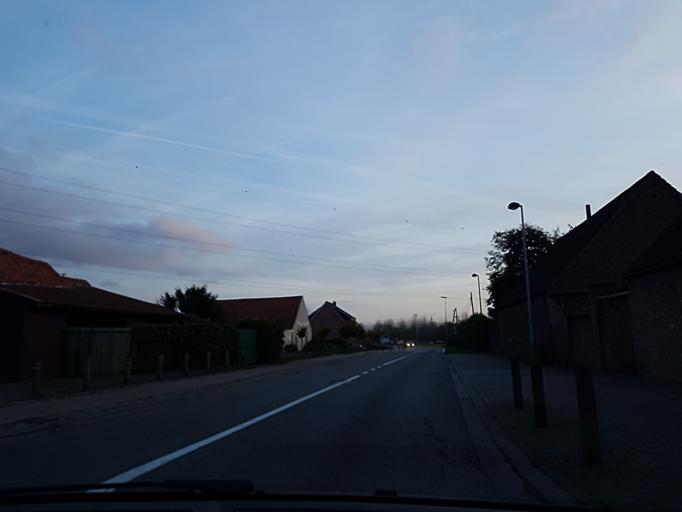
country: BE
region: Flanders
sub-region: Provincie Antwerpen
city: Ranst
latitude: 51.1725
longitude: 4.5634
